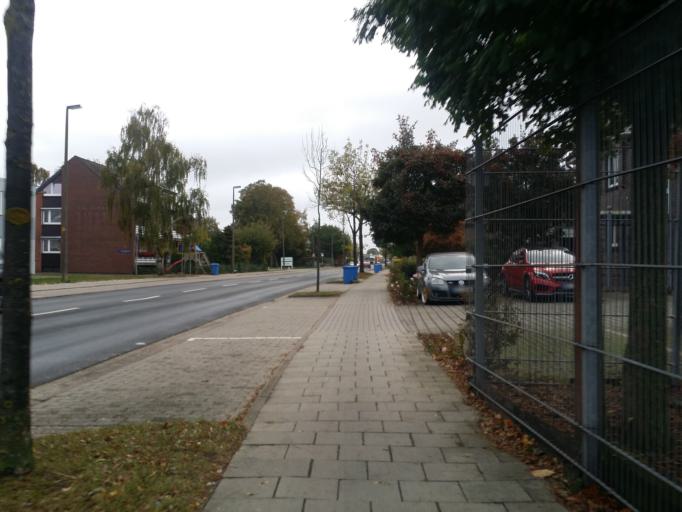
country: DE
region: Lower Saxony
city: Delmenhorst
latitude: 53.0243
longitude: 8.6379
